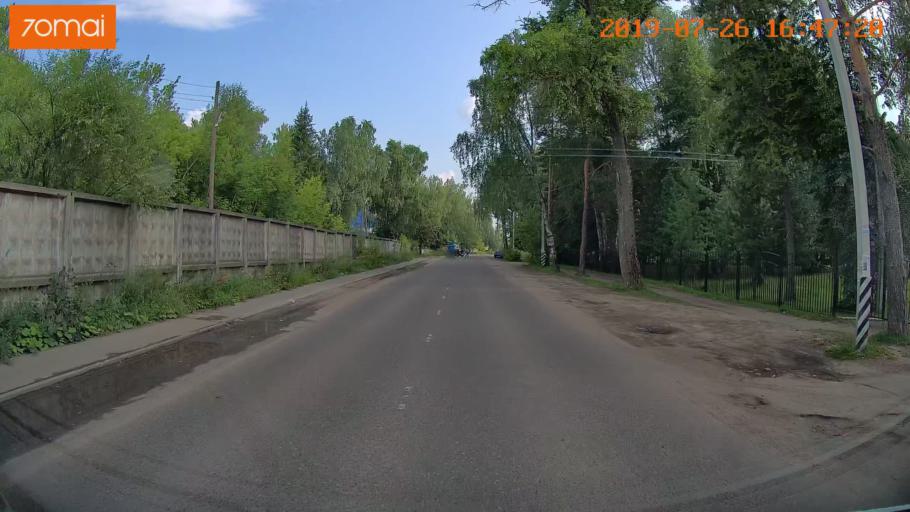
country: RU
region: Ivanovo
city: Bogorodskoye
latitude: 57.0422
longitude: 41.0118
